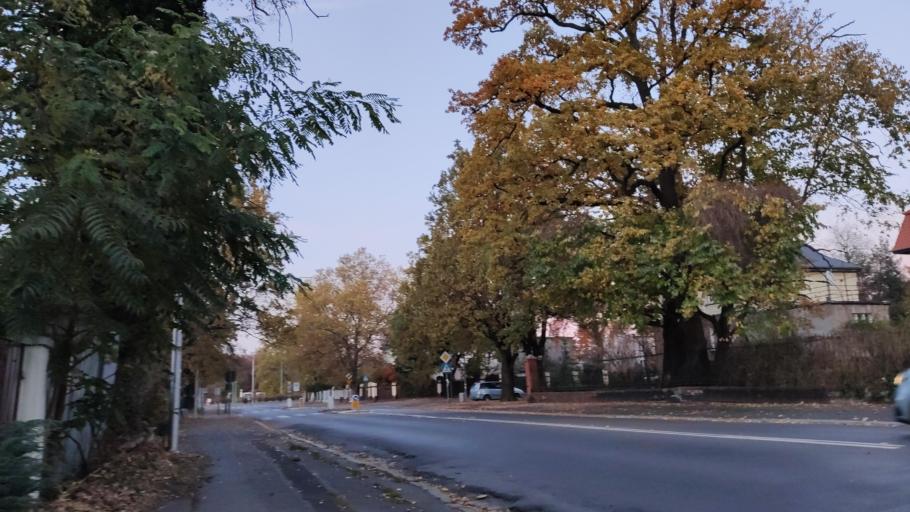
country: PL
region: Lower Silesian Voivodeship
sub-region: Powiat wroclawski
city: Wroclaw
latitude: 51.0836
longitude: 17.0176
